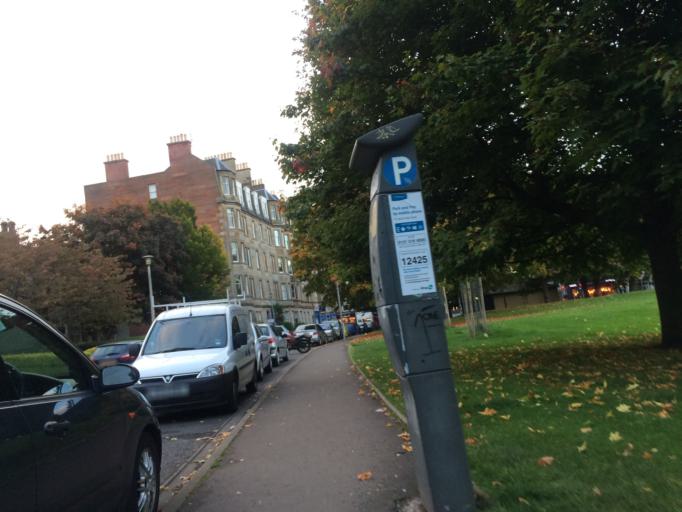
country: GB
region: Scotland
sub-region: Edinburgh
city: Edinburgh
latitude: 55.9366
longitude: -3.2056
